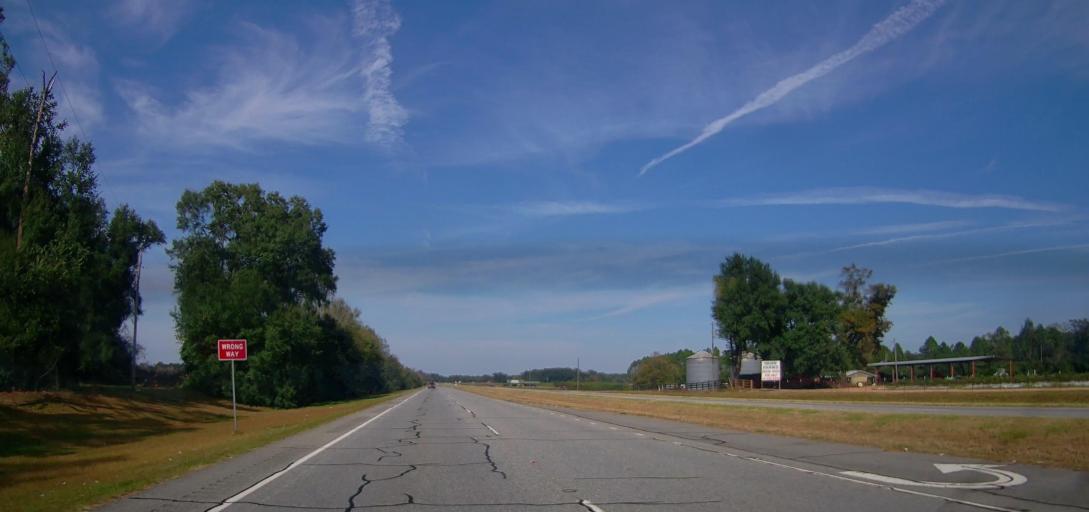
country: US
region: Georgia
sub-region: Mitchell County
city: Camilla
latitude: 31.3251
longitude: -84.1729
